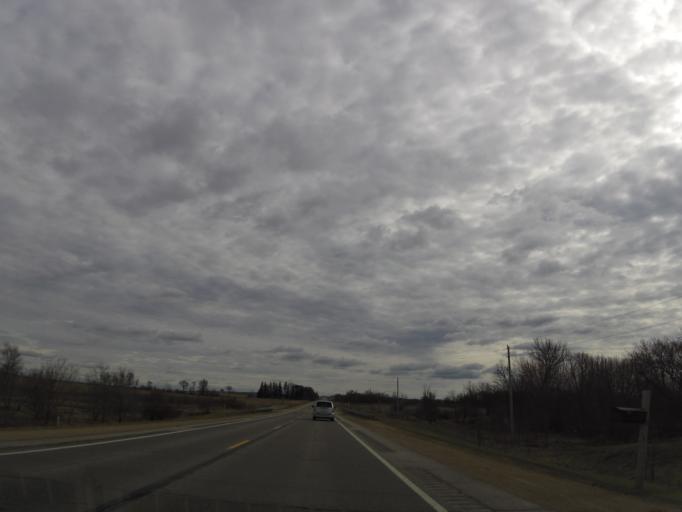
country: US
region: Iowa
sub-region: Chickasaw County
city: New Hampton
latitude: 43.2105
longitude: -92.2984
